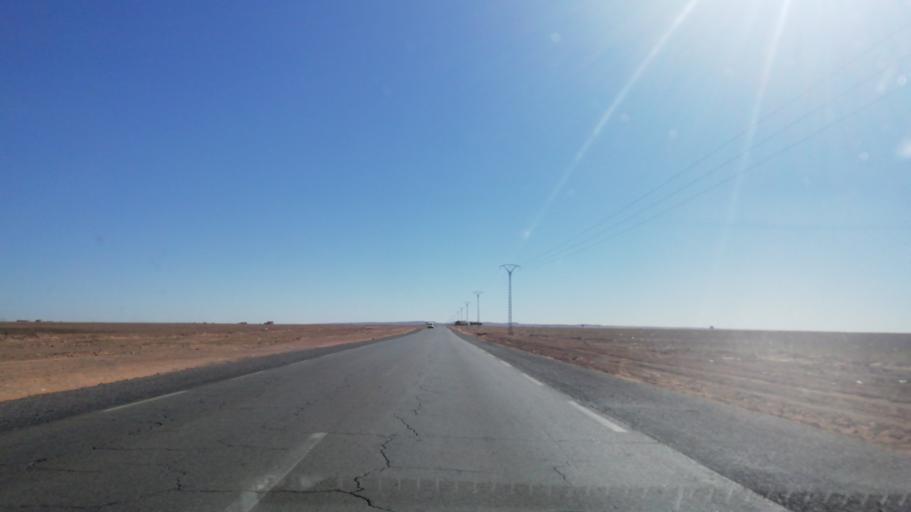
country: DZ
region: Saida
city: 'Ain el Hadjar
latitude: 34.0164
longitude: 0.1099
